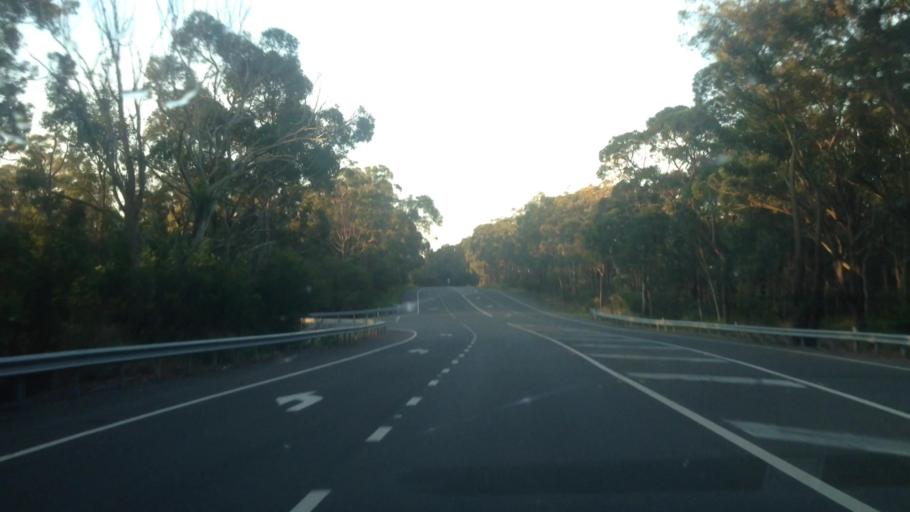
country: AU
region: New South Wales
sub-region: Wyong Shire
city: Kingfisher Shores
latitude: -33.1550
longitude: 151.4789
